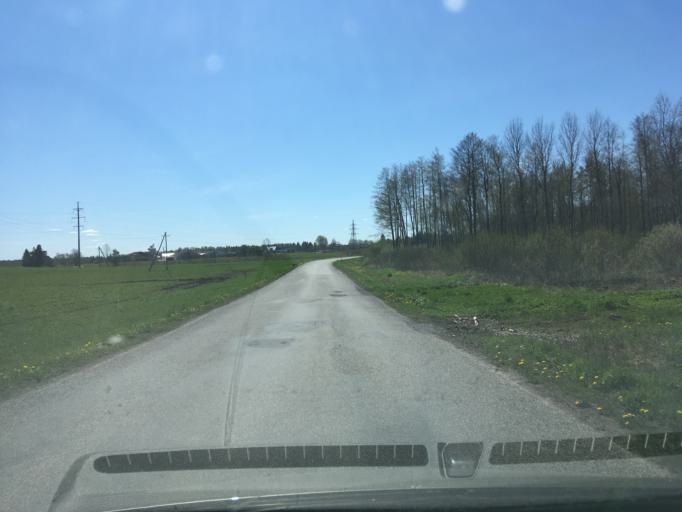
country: EE
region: Harju
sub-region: Raasiku vald
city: Arukula
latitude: 59.3866
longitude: 25.0797
